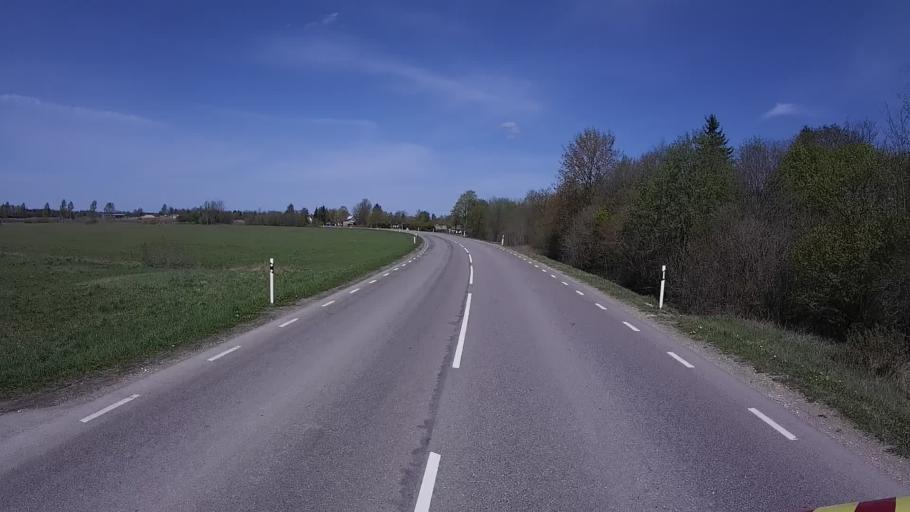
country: EE
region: Harju
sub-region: Keila linn
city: Keila
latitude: 59.3023
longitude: 24.3248
